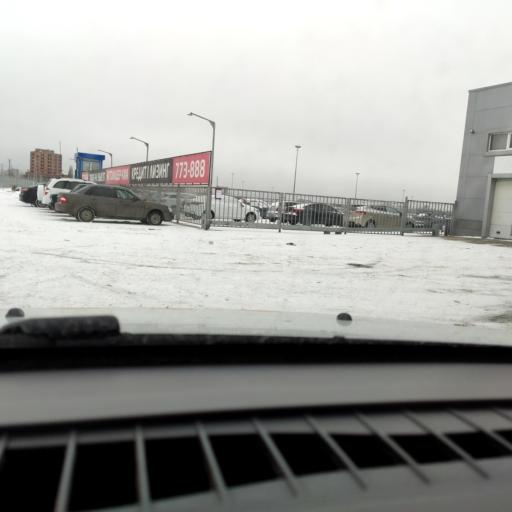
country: RU
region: Samara
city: Tol'yatti
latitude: 53.5580
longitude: 49.3510
